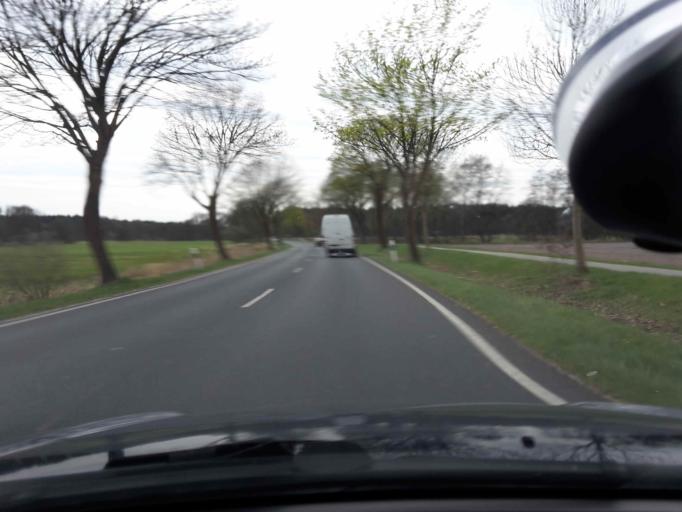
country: DE
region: Lower Saxony
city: Jesteburg
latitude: 53.2986
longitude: 9.9313
